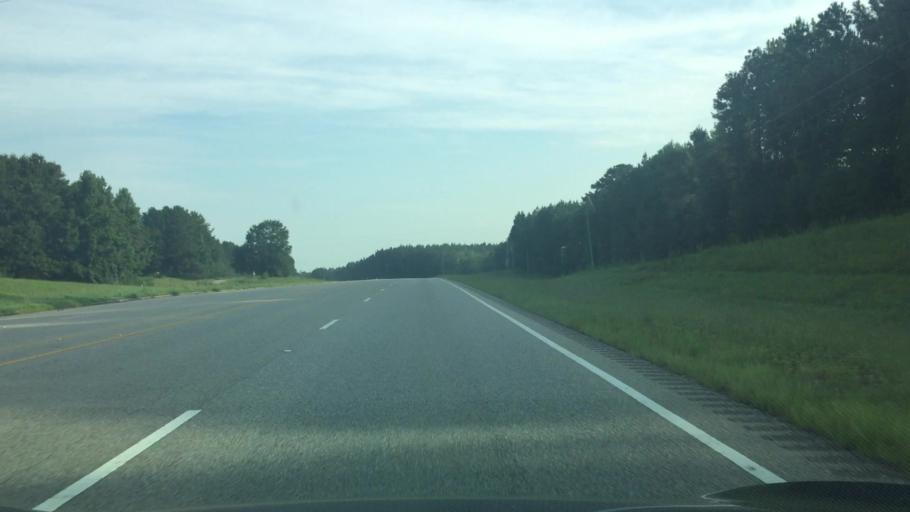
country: US
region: Alabama
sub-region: Covington County
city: Andalusia
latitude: 31.4354
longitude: -86.6117
